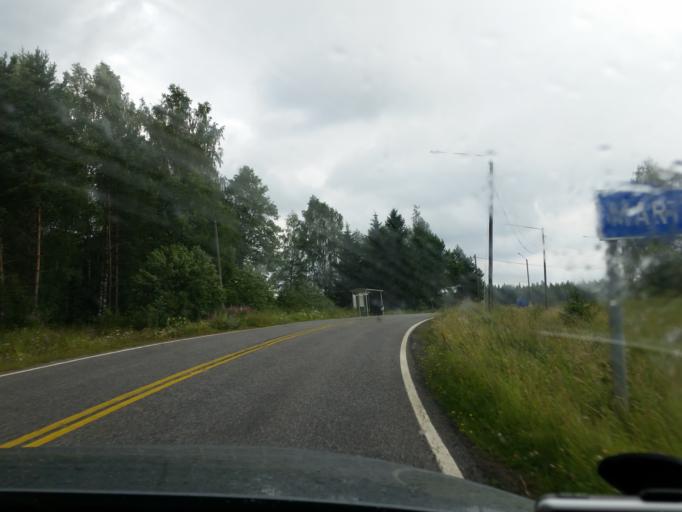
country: FI
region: Uusimaa
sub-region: Helsinki
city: Kaerkoelae
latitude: 60.5073
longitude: 23.9642
